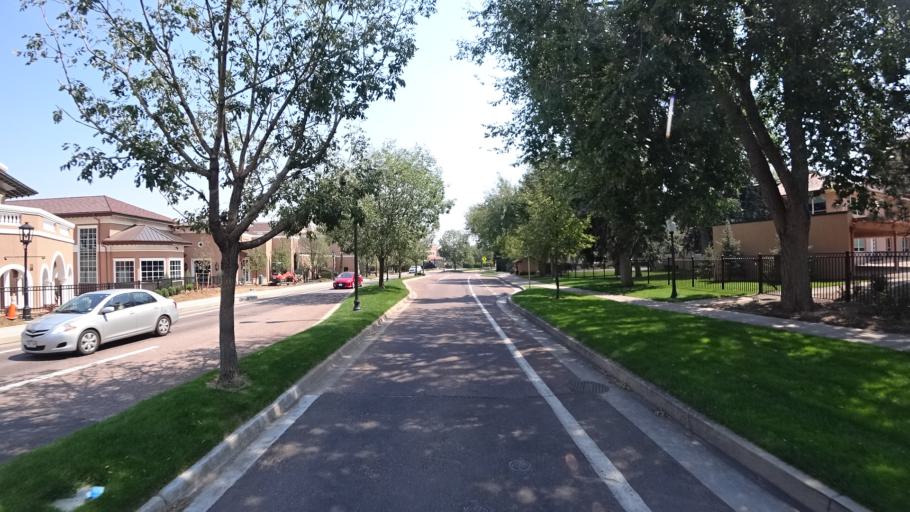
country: US
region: Colorado
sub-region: El Paso County
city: Colorado Springs
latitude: 38.7926
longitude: -104.8506
